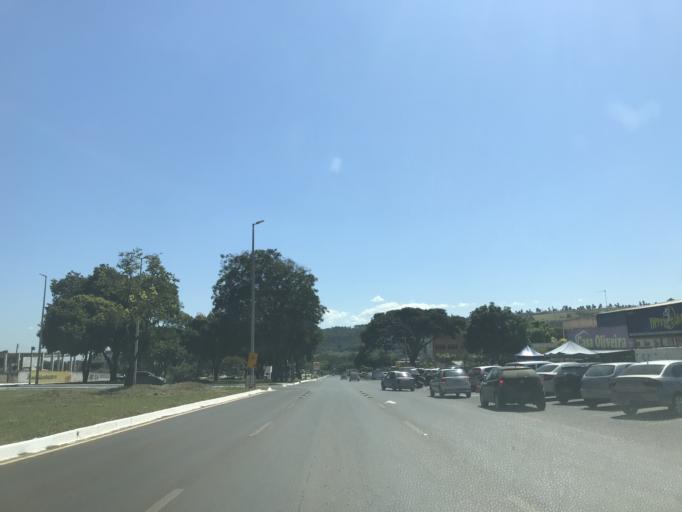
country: BR
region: Federal District
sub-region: Brasilia
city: Brasilia
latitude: -15.6485
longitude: -47.7854
